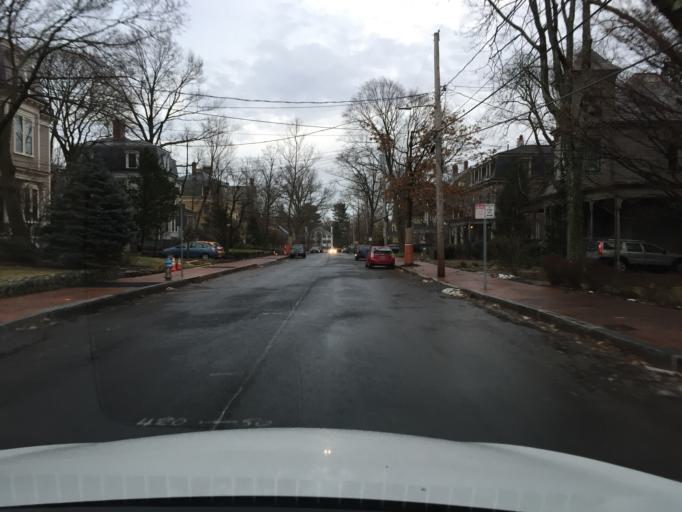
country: US
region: Massachusetts
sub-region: Middlesex County
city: Cambridge
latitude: 42.3790
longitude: -71.1393
